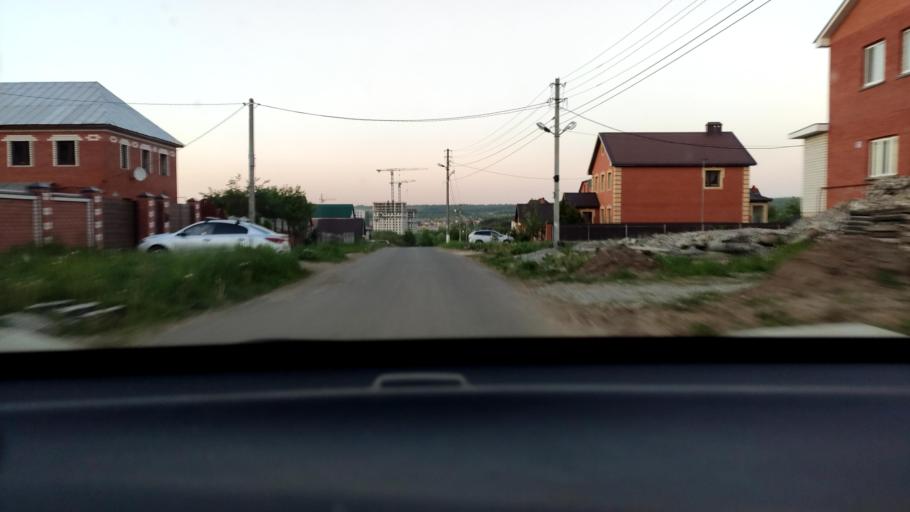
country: RU
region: Tatarstan
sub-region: Gorod Kazan'
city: Kazan
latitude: 55.7844
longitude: 49.2439
